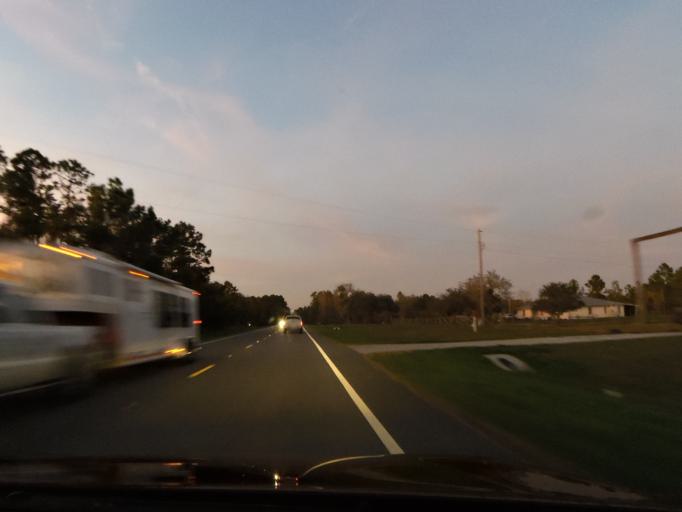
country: US
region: Florida
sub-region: Volusia County
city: De Leon Springs
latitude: 29.1988
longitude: -81.3138
